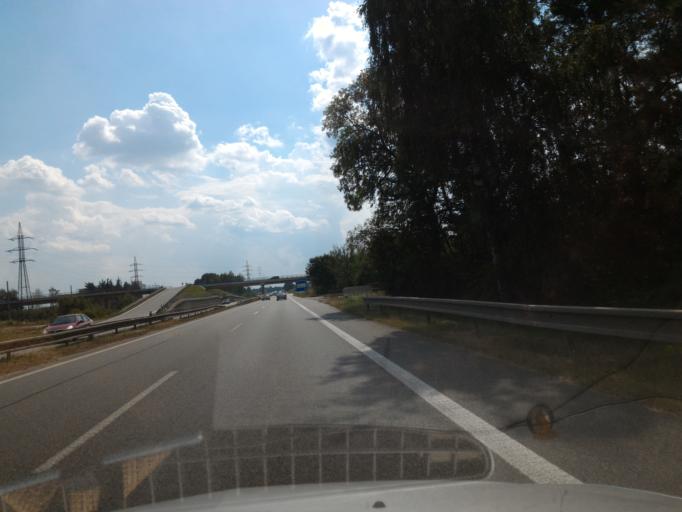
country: CZ
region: Vysocina
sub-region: Okres Jihlava
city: Jihlava
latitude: 49.4379
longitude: 15.6022
